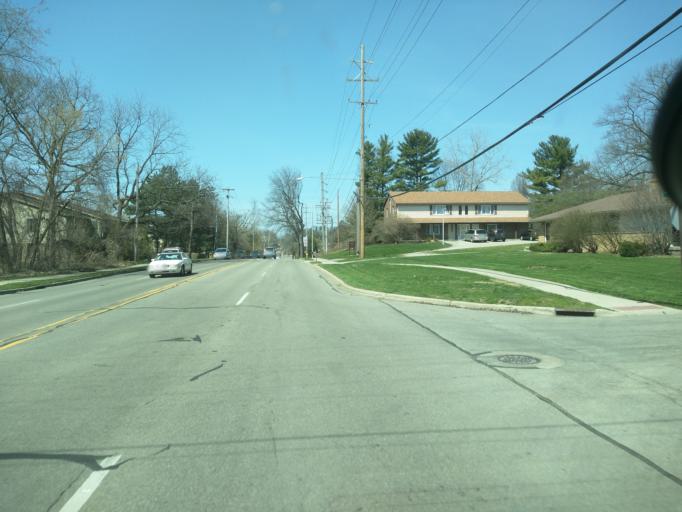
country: US
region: Michigan
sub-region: Kent County
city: East Grand Rapids
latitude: 42.9270
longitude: -85.5788
